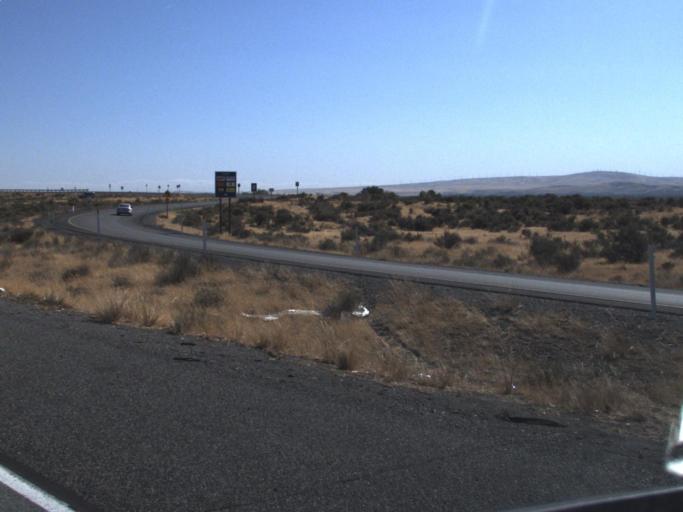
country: US
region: Washington
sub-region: Franklin County
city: West Pasco
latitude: 46.2668
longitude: -119.1866
